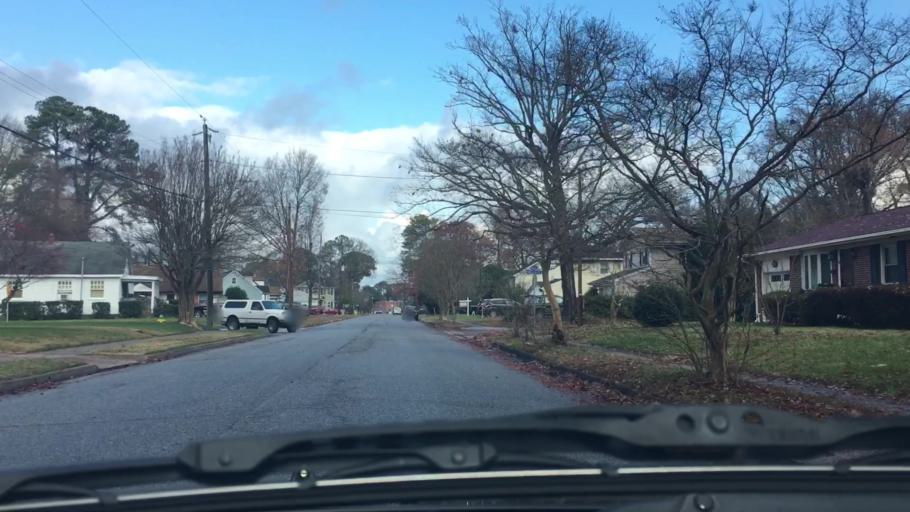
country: US
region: Virginia
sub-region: City of Norfolk
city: Norfolk
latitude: 36.9243
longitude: -76.2460
